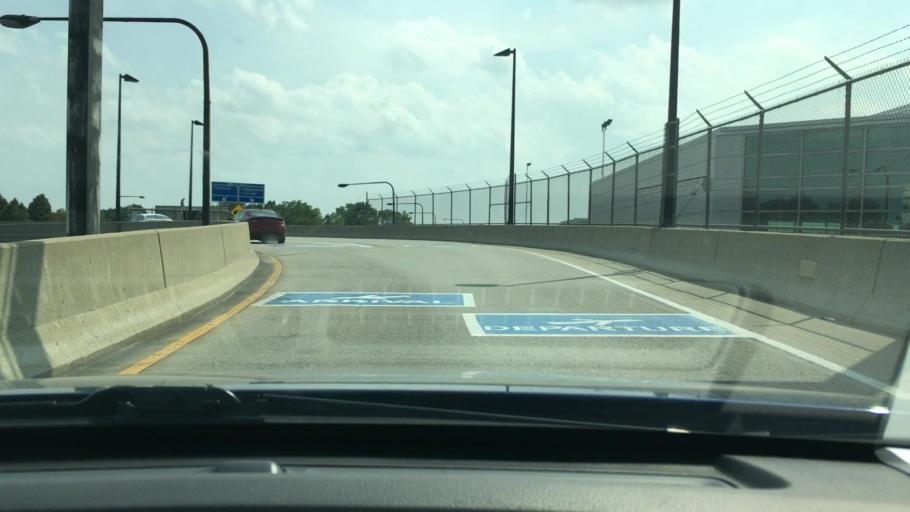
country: US
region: Illinois
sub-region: Cook County
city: Hometown
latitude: 41.7861
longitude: -87.7416
